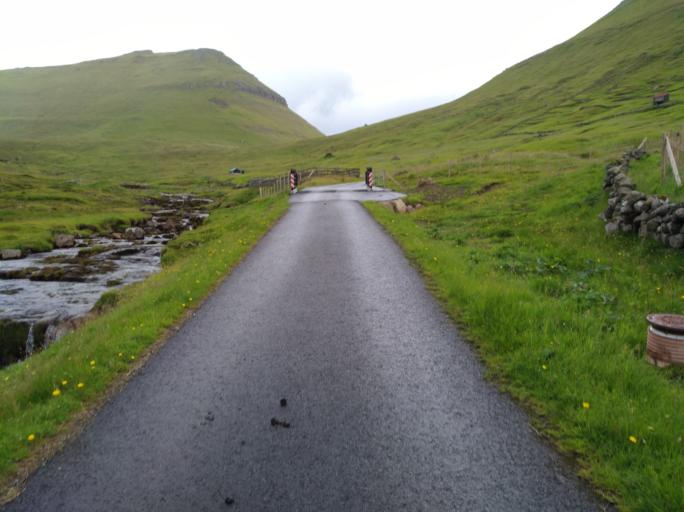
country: FO
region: Eysturoy
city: Fuglafjordur
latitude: 62.2790
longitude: -6.8607
